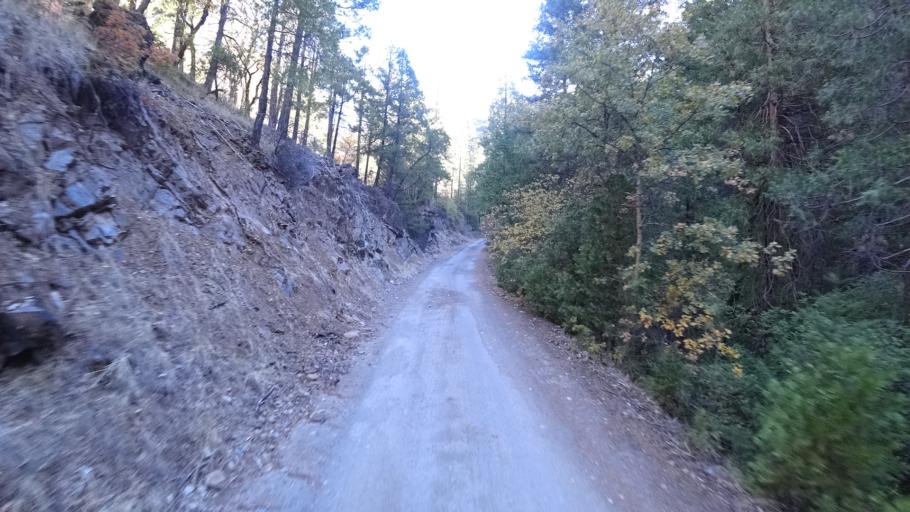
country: US
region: California
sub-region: Trinity County
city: Weaverville
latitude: 41.1463
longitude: -123.1370
